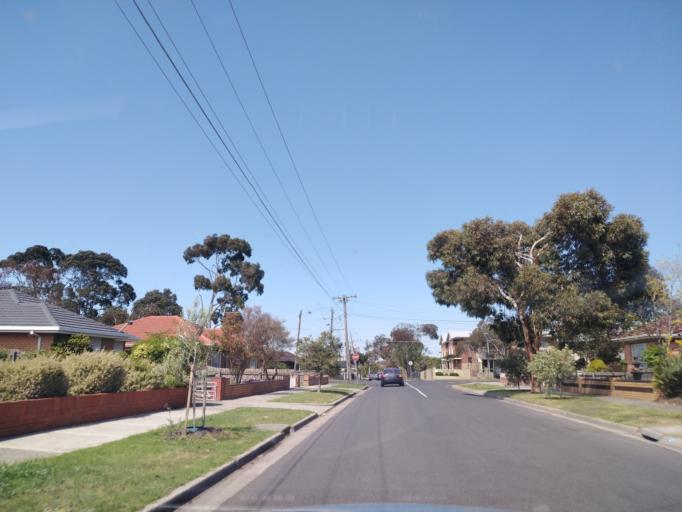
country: AU
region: Victoria
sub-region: Hobsons Bay
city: Altona North
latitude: -37.8385
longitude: 144.8532
